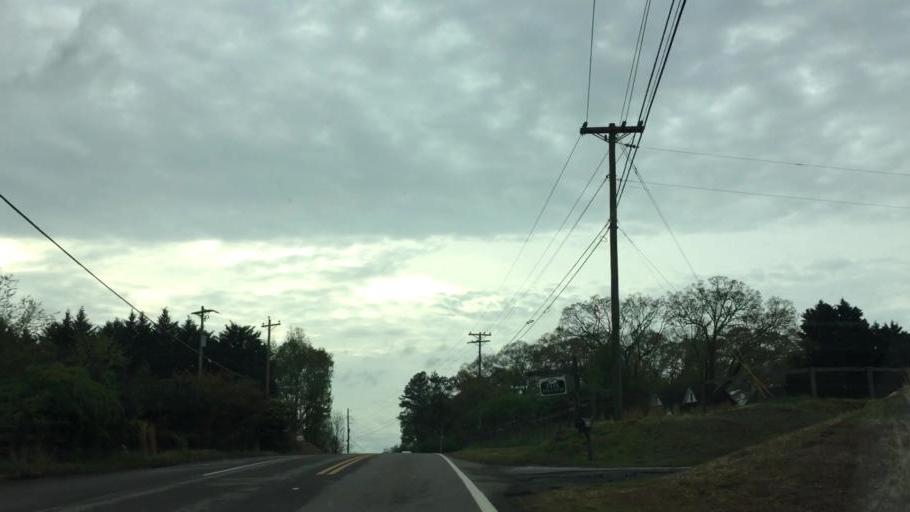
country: US
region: Georgia
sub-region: Fulton County
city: Milton
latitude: 34.1970
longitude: -84.3507
